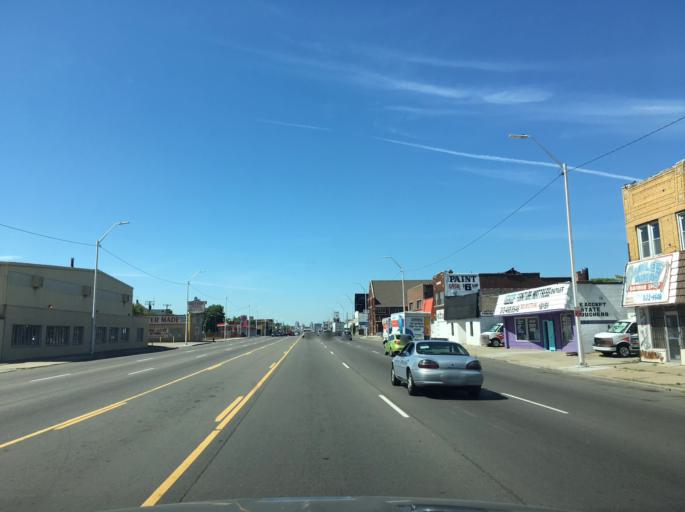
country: US
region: Michigan
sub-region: Wayne County
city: Hamtramck
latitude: 42.3969
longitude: -83.0028
